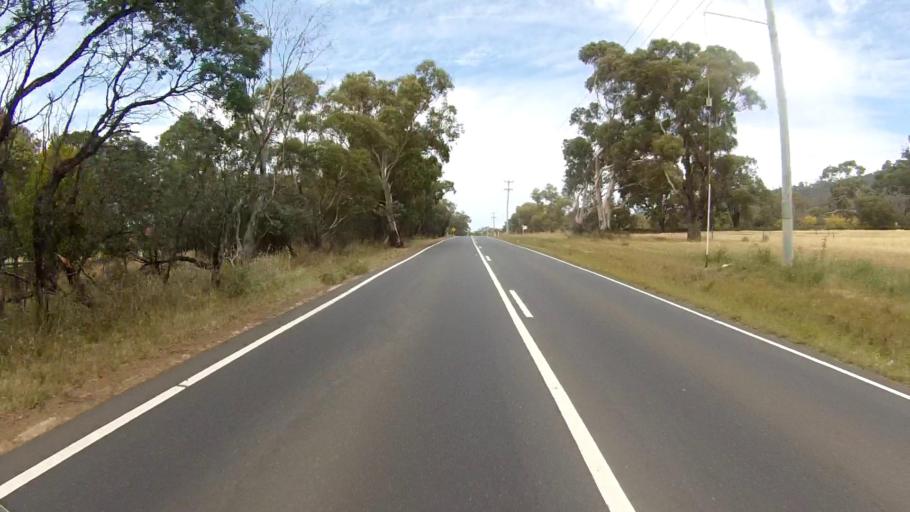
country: AU
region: Tasmania
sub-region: Clarence
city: Acton Park
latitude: -42.8854
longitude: 147.4832
